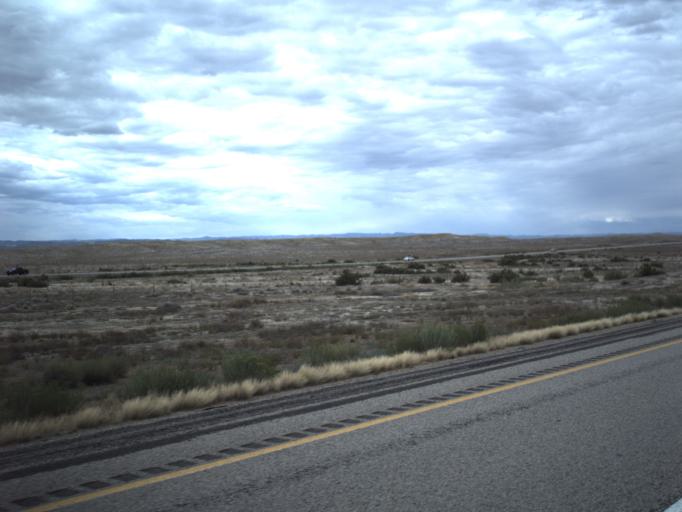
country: US
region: Utah
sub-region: Grand County
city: Moab
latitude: 38.9646
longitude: -109.3722
